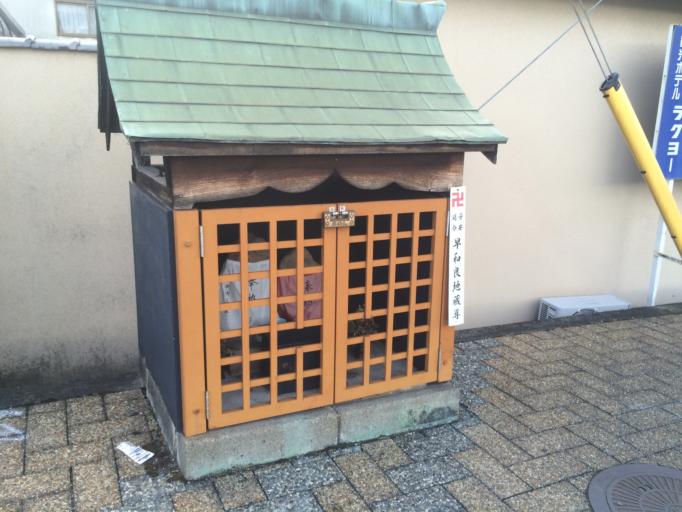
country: JP
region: Nara
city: Nara-shi
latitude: 34.6736
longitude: 135.8345
